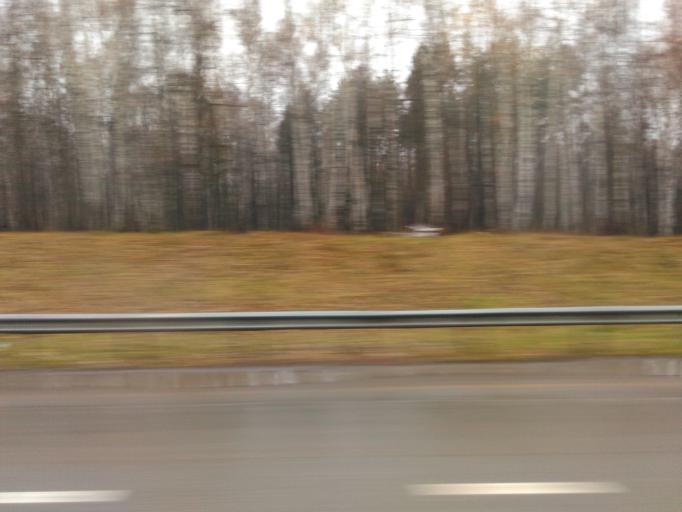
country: RU
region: Tatarstan
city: Osinovo
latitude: 55.8368
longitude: 48.8505
